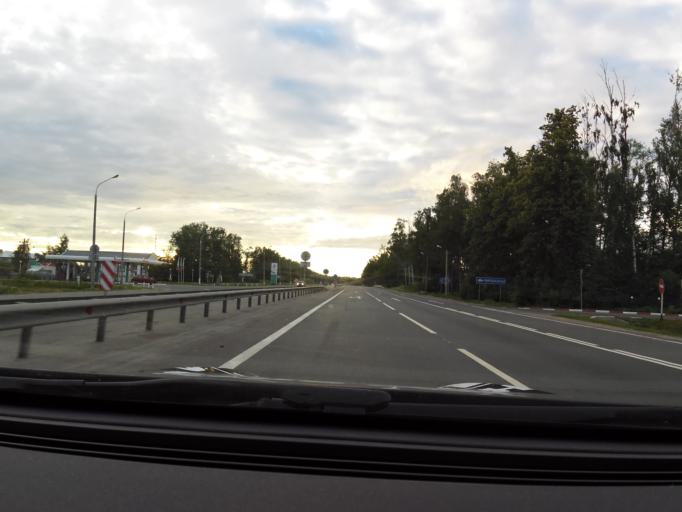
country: RU
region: Chuvashia
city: Kugesi
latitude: 56.0071
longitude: 47.3193
